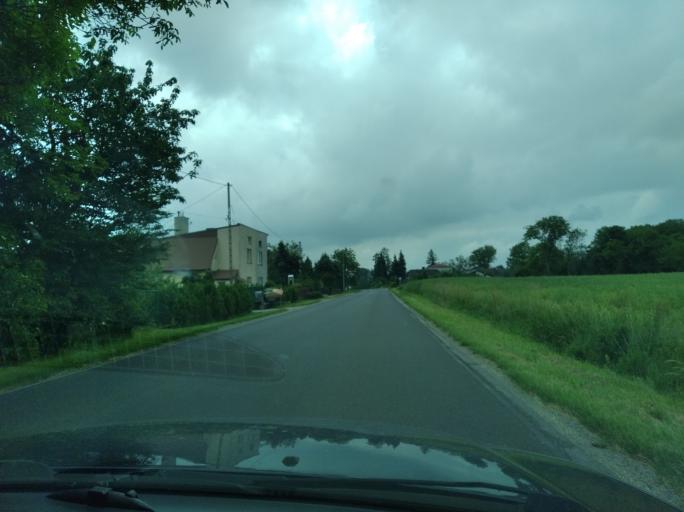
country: PL
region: Subcarpathian Voivodeship
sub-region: Powiat jaroslawski
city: Pawlosiow
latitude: 50.0196
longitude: 22.6402
